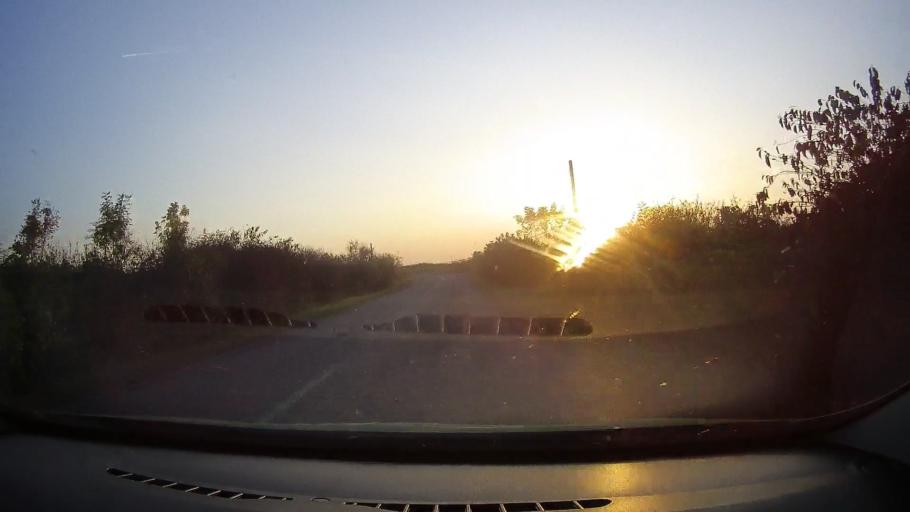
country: RO
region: Arad
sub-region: Comuna Sicula
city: Sicula
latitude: 46.4190
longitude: 21.7401
